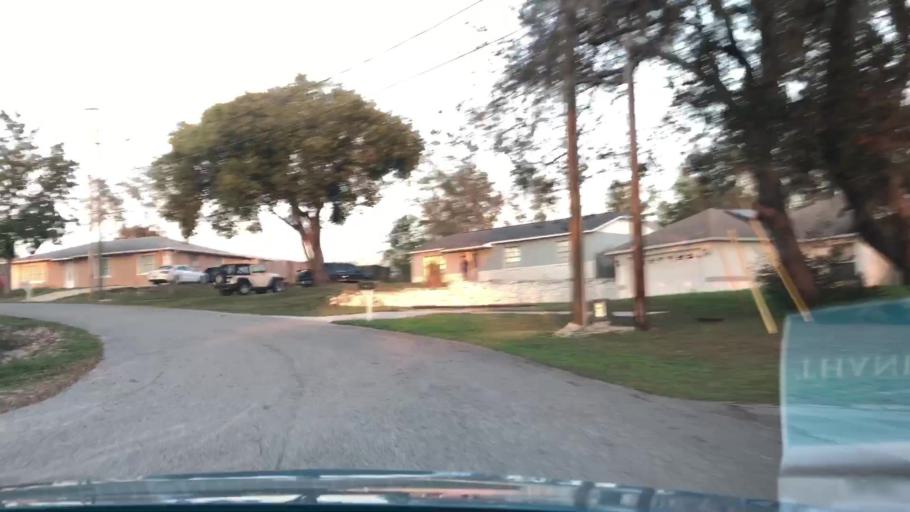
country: US
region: Florida
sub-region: Volusia County
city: Deltona
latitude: 28.8744
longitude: -81.2493
